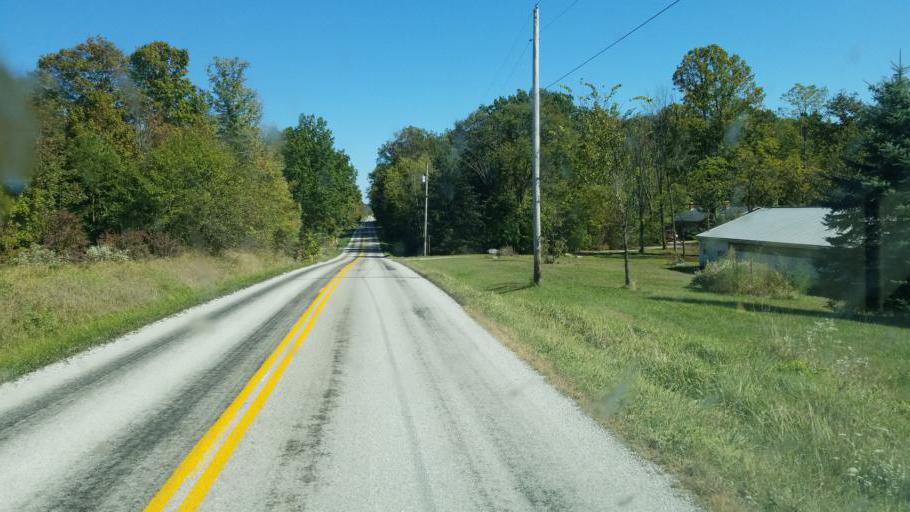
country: US
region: Ohio
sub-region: Ashland County
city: Ashland
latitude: 40.9928
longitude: -82.2794
